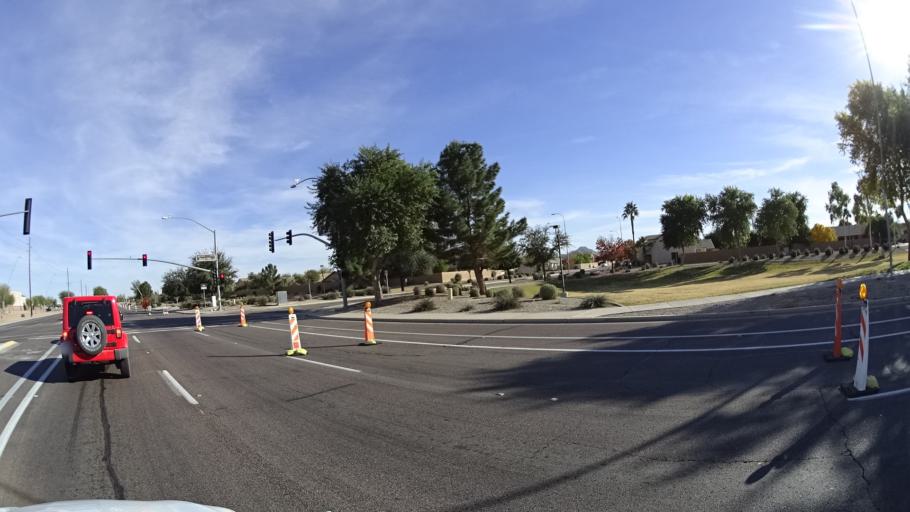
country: US
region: Arizona
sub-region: Maricopa County
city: Sun Lakes
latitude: 33.2192
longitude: -111.7602
